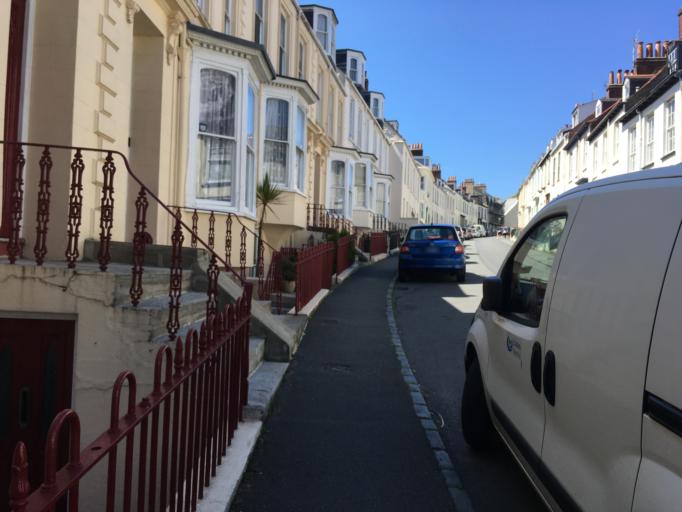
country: GG
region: St Peter Port
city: Saint Peter Port
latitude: 49.4543
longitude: -2.5457
